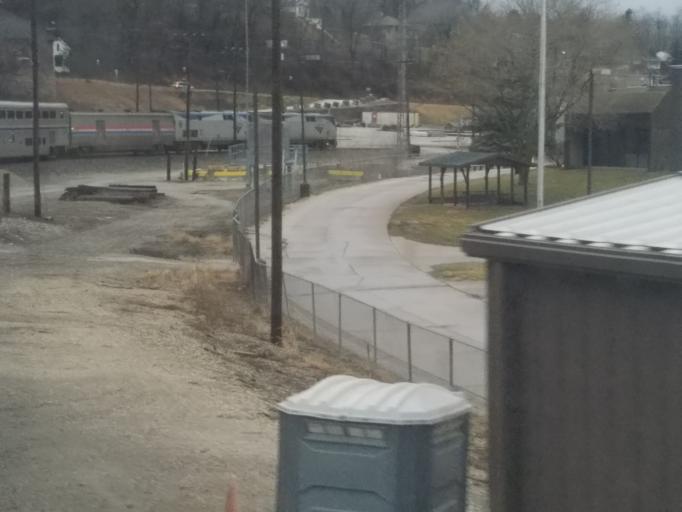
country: US
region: Iowa
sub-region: Des Moines County
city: Burlington
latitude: 40.7970
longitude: -91.0962
